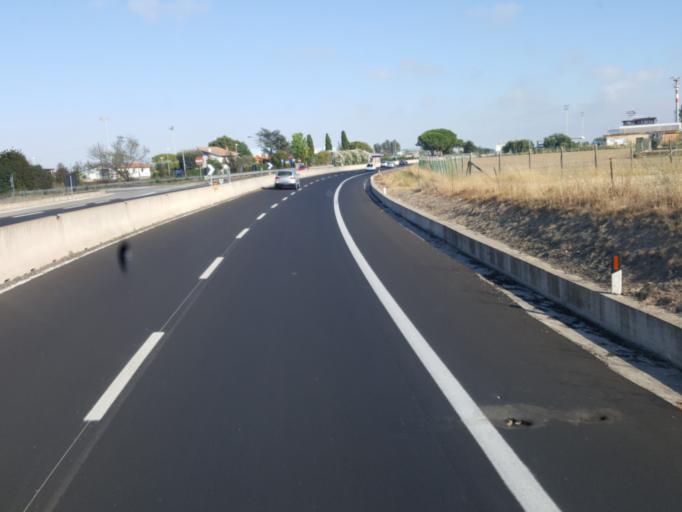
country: IT
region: Latium
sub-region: Provincia di Viterbo
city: Montalto di Castro
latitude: 42.3455
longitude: 11.6133
